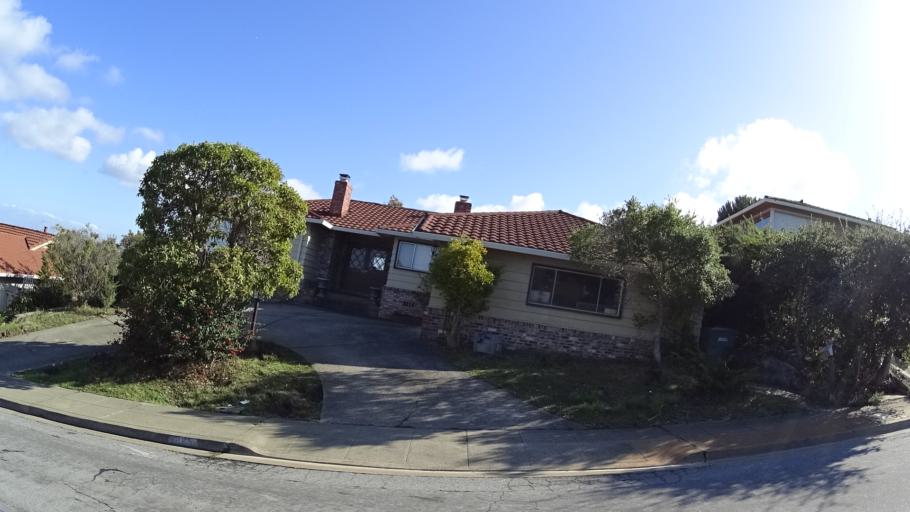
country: US
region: California
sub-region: San Mateo County
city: Millbrae
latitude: 37.5893
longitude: -122.3980
